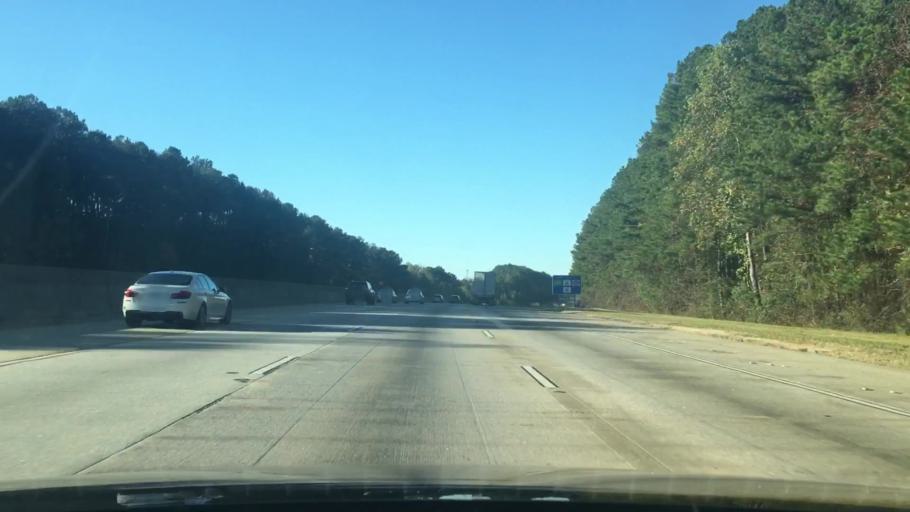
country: US
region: Georgia
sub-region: Fulton County
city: Palmetto
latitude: 33.4558
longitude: -84.6780
